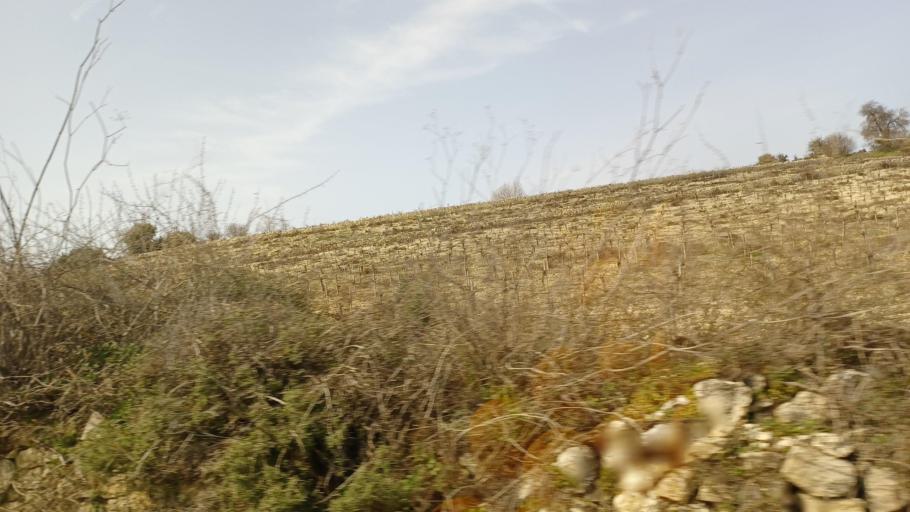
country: CY
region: Limassol
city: Pachna
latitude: 34.8120
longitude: 32.7686
